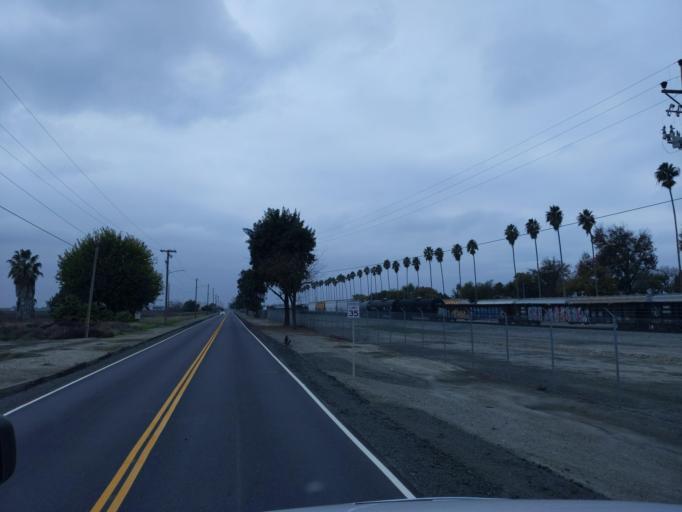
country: US
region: California
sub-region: San Joaquin County
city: Country Club
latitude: 37.9483
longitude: -121.3487
